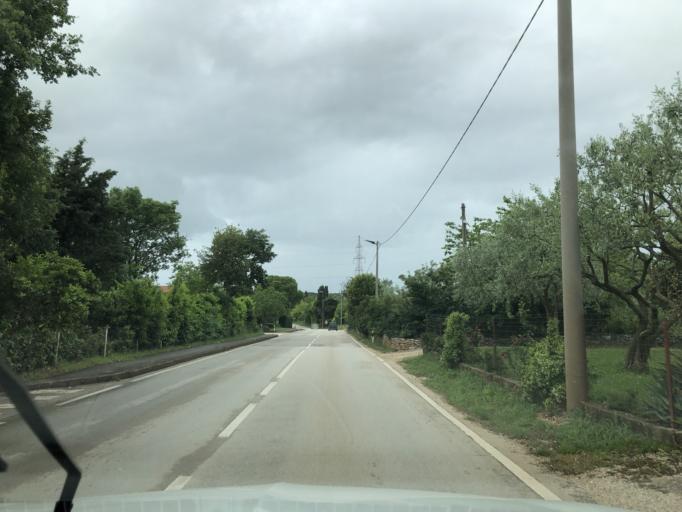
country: SI
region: Piran-Pirano
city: Seca
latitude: 45.4506
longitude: 13.5798
